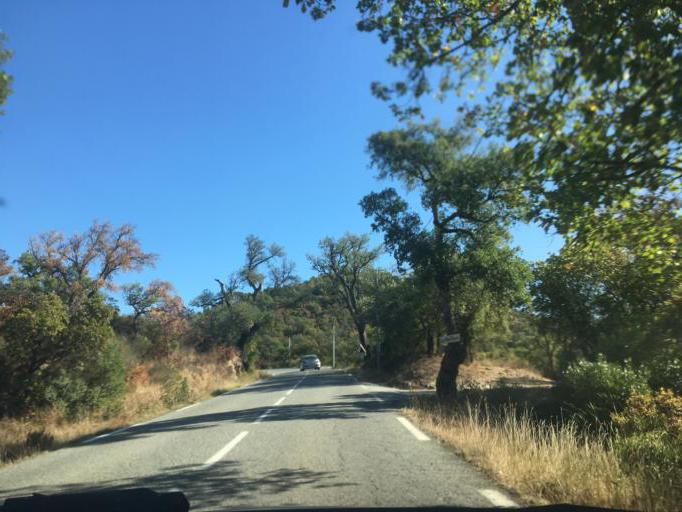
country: FR
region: Provence-Alpes-Cote d'Azur
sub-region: Departement du Var
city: La Garde-Freinet
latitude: 43.3328
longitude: 6.4301
